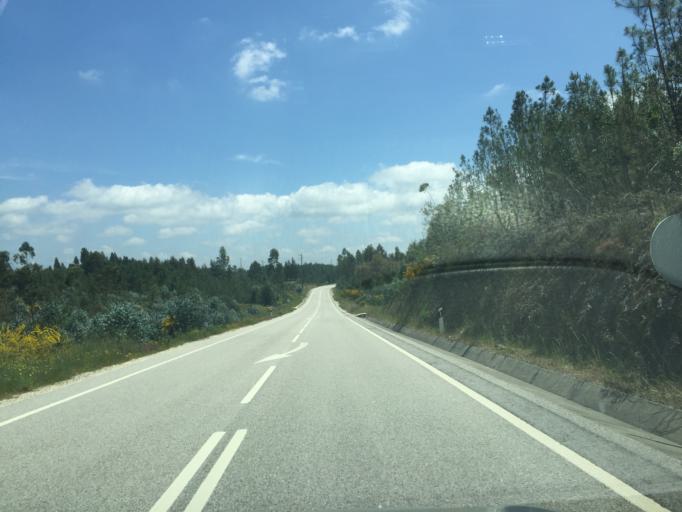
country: PT
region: Castelo Branco
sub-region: Vila de Rei
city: Vila de Rei
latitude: 39.7072
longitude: -8.1333
